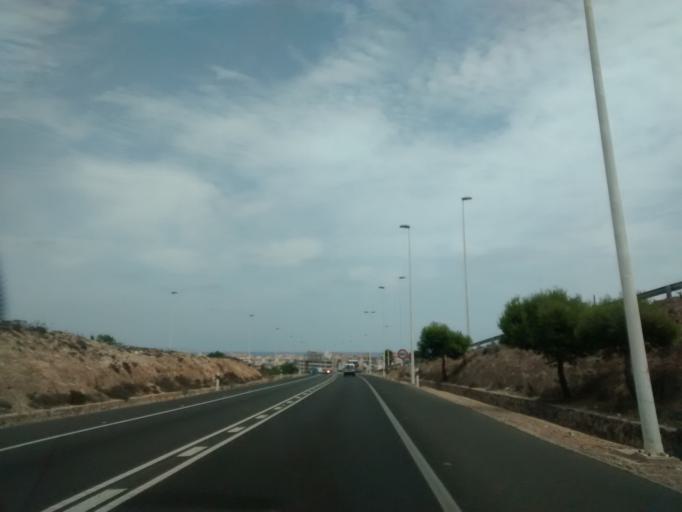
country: ES
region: Valencia
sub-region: Provincia de Alicante
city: Torrevieja
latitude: 38.0108
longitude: -0.6648
